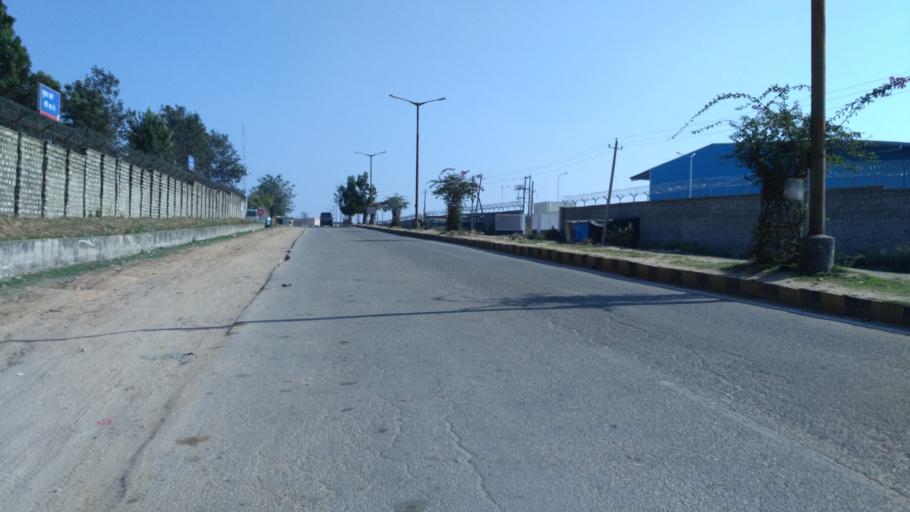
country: IN
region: Karnataka
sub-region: Hassan
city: Hassan
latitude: 12.9848
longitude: 76.1177
